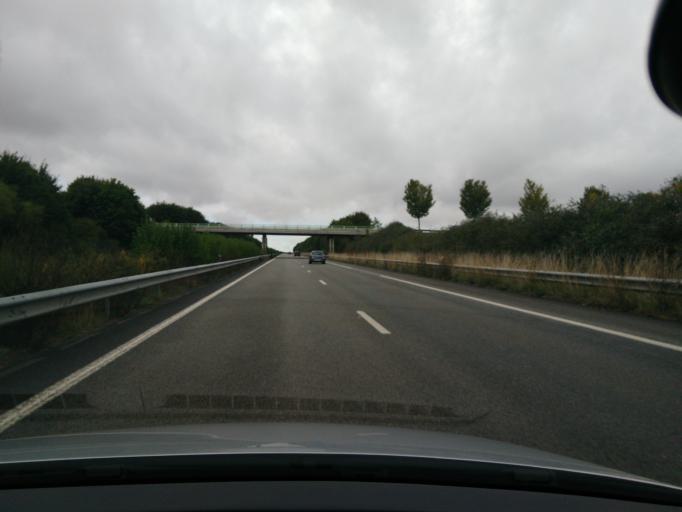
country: FR
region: Ile-de-France
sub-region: Departement des Yvelines
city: Houdan
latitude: 48.7826
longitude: 1.6076
